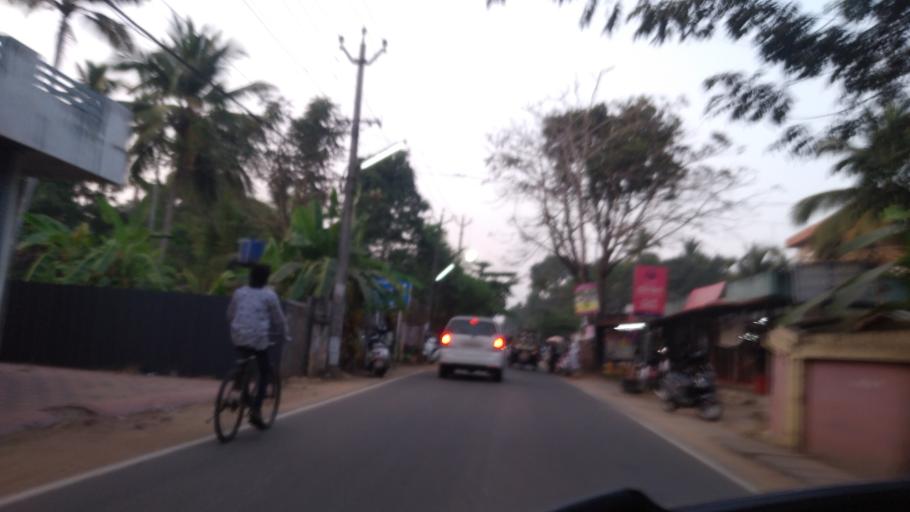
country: IN
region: Kerala
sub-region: Thrissur District
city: Kodungallur
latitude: 10.1394
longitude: 76.2299
